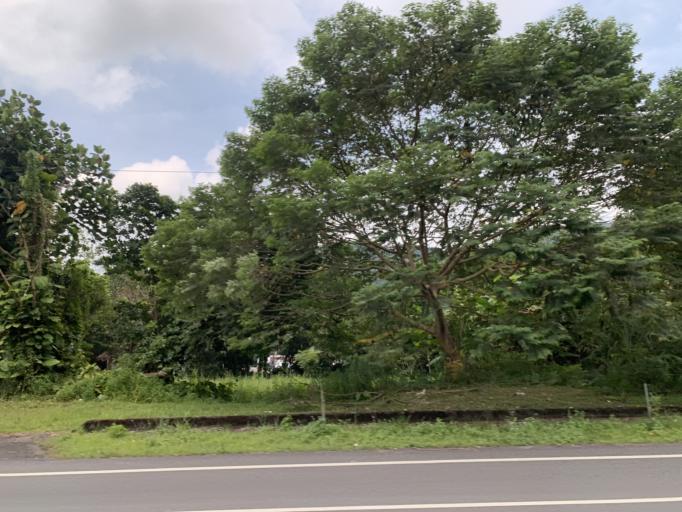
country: TW
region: Taiwan
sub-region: Hualien
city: Hualian
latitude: 23.9350
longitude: 121.5061
